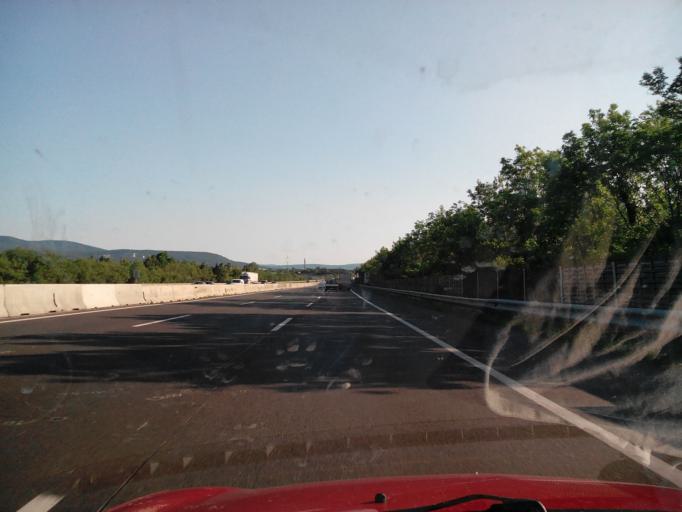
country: AT
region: Lower Austria
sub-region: Politischer Bezirk Baden
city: Leobersdorf
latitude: 47.9234
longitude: 16.2089
